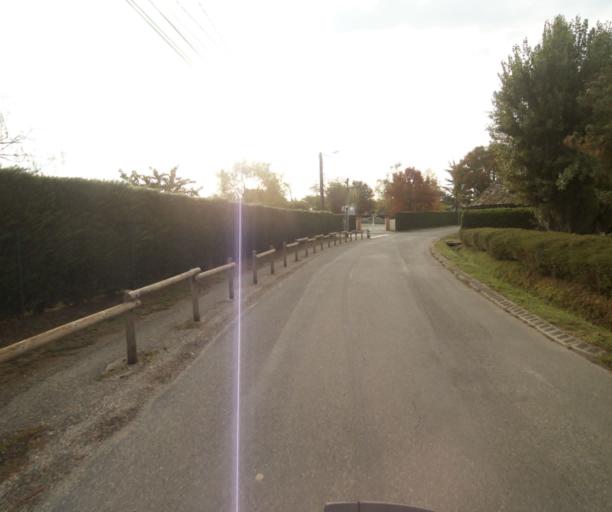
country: FR
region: Midi-Pyrenees
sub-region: Departement du Tarn-et-Garonne
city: Montech
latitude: 43.9545
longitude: 1.2389
